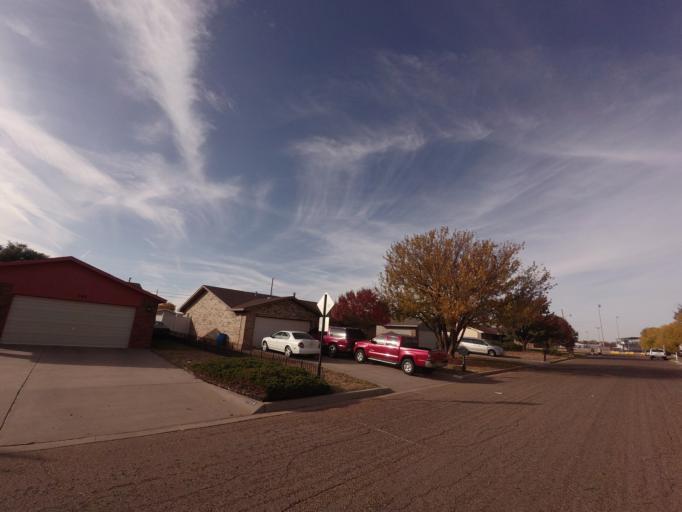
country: US
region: New Mexico
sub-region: Curry County
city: Clovis
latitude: 34.4224
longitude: -103.2304
